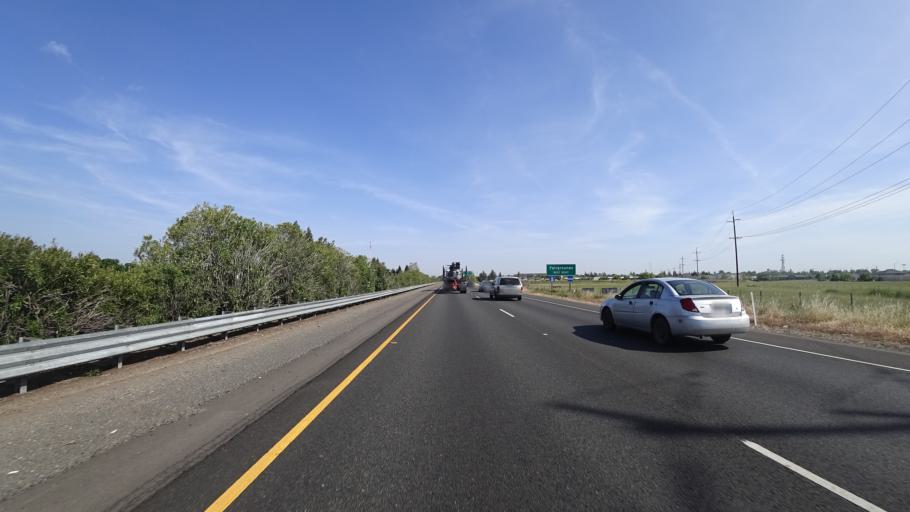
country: US
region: California
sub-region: Butte County
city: Chico
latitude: 39.7217
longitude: -121.8060
